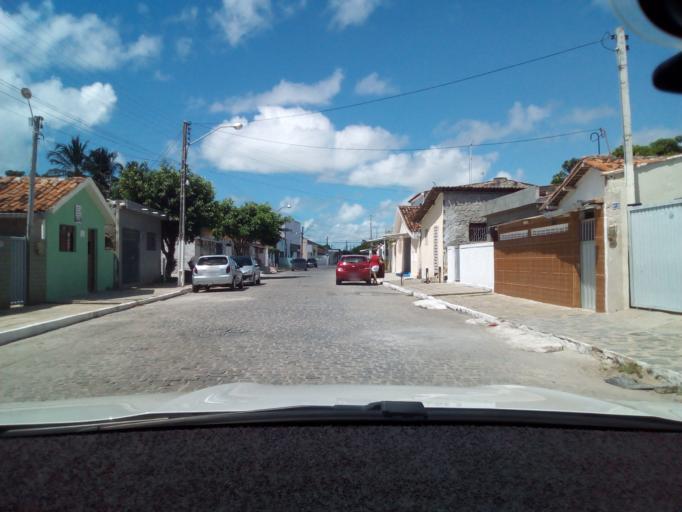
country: BR
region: Paraiba
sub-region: Cabedelo
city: Cabedelo
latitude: -6.9769
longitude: -34.8342
